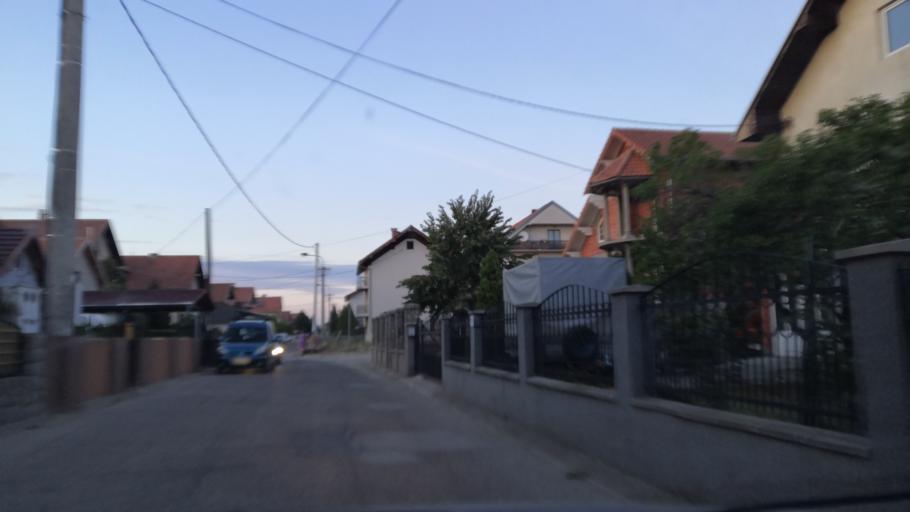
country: RS
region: Central Serbia
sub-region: Borski Okrug
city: Negotin
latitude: 44.2404
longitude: 22.5292
